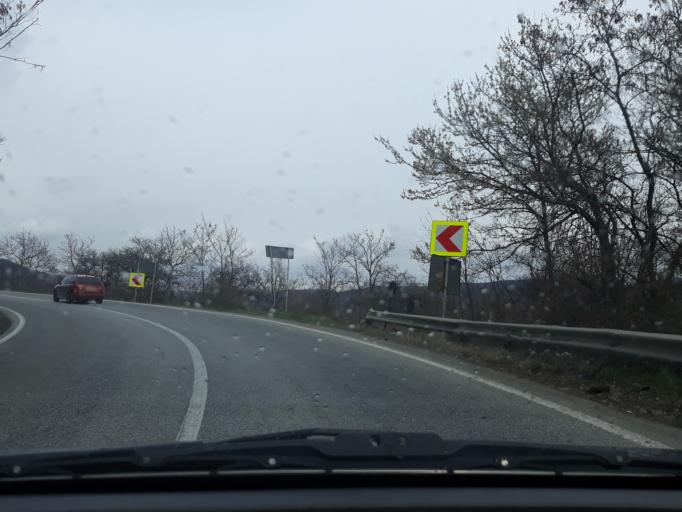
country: RO
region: Harghita
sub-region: Comuna Lupeni
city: Lupeni
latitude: 46.4077
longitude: 25.2171
